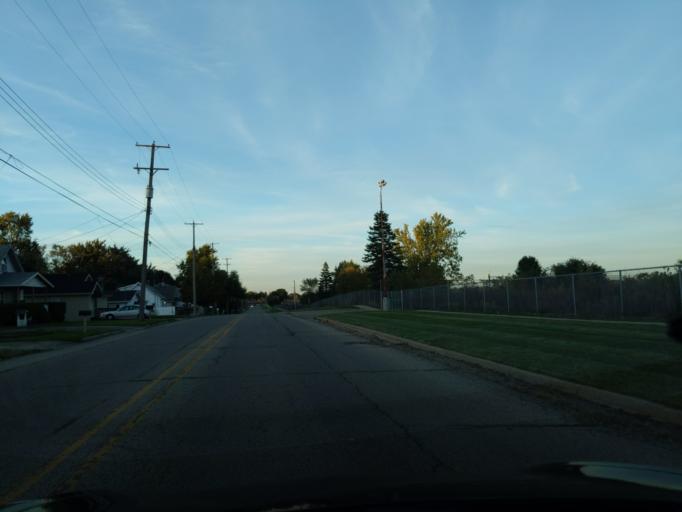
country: US
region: Michigan
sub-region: Ingham County
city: Edgemont Park
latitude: 42.7352
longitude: -84.5876
